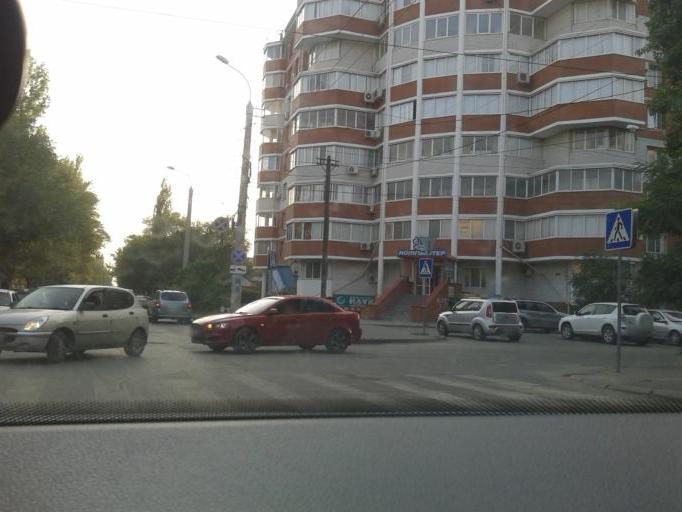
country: RU
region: Volgograd
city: Volgograd
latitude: 48.7016
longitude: 44.5013
